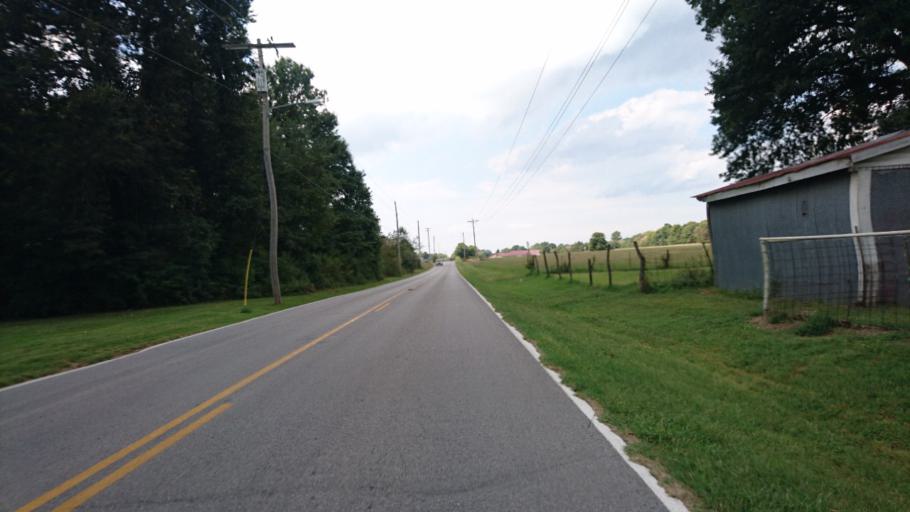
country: US
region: Missouri
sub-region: Greene County
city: Springfield
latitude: 37.1976
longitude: -93.3637
